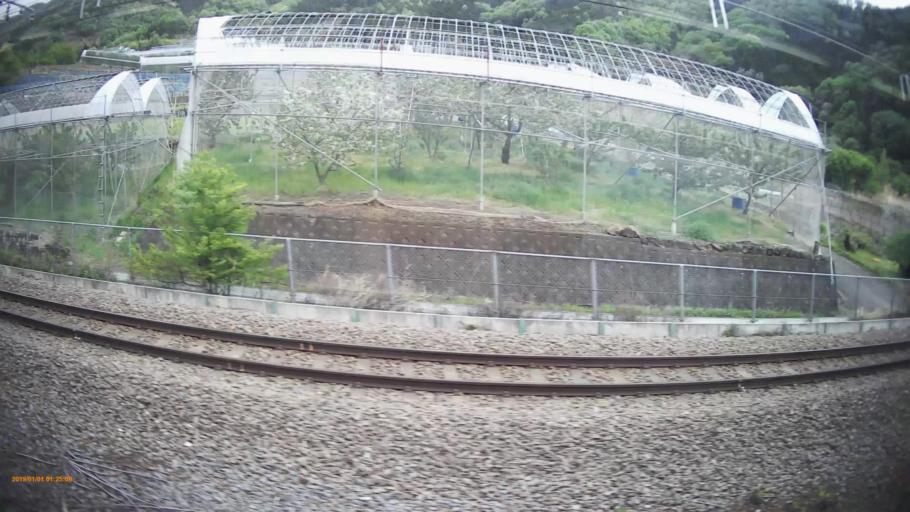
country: JP
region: Yamanashi
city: Enzan
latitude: 35.6933
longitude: 138.7439
